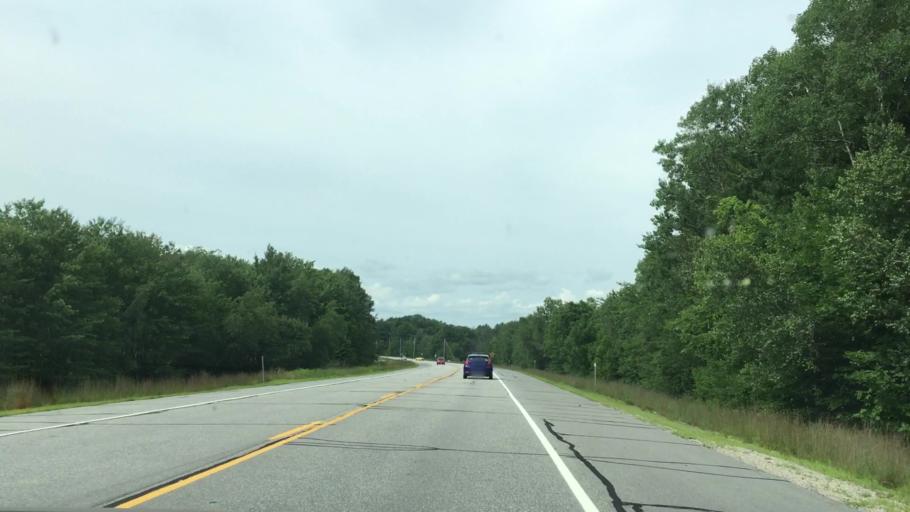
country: US
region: New Hampshire
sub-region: Hillsborough County
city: Hillsborough
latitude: 43.0817
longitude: -71.9173
